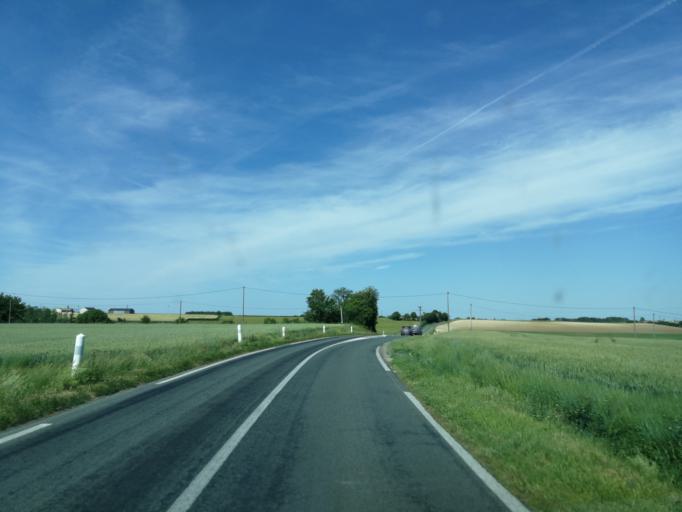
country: FR
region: Poitou-Charentes
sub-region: Departement de la Vienne
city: Loudun
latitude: 47.0228
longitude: 0.1045
